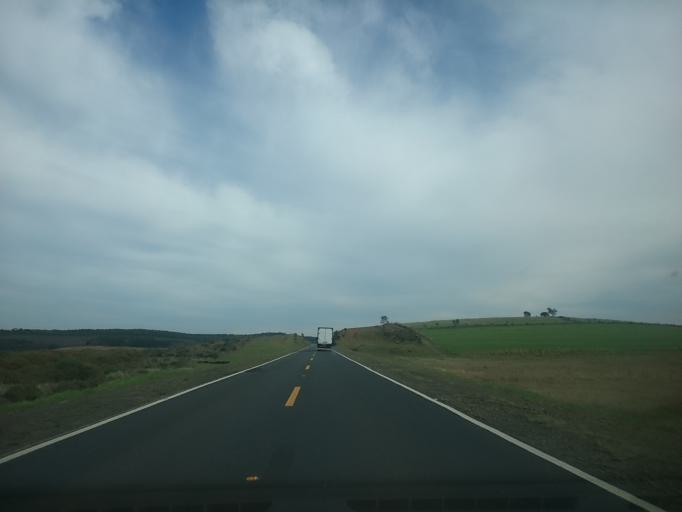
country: BR
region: Rio Grande do Sul
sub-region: Vacaria
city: Estrela
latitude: -28.1608
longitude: -50.6663
